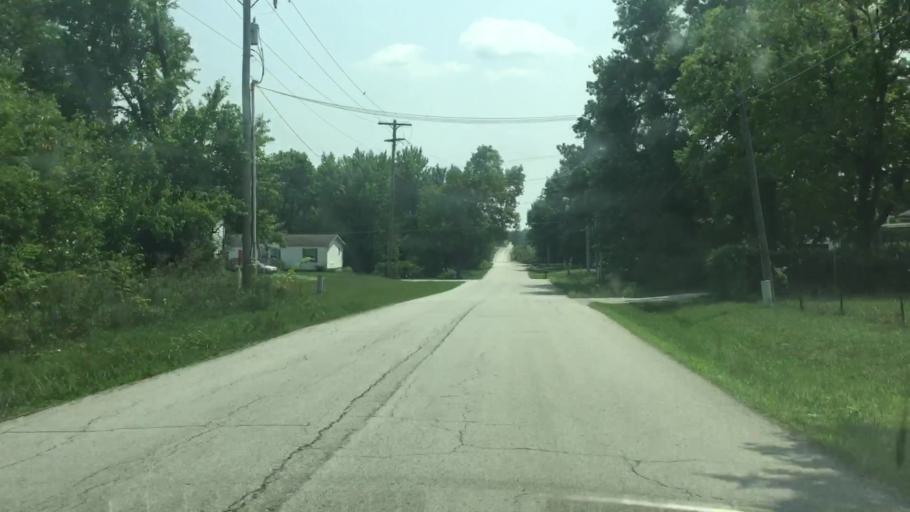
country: US
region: Kansas
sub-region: Douglas County
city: Baldwin City
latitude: 38.7738
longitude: -95.2049
